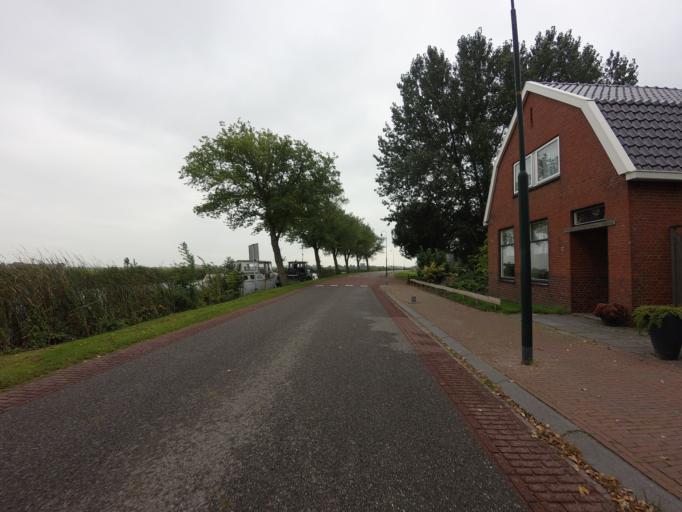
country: NL
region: Friesland
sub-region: Sudwest Fryslan
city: Workum
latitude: 53.0125
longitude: 5.4770
